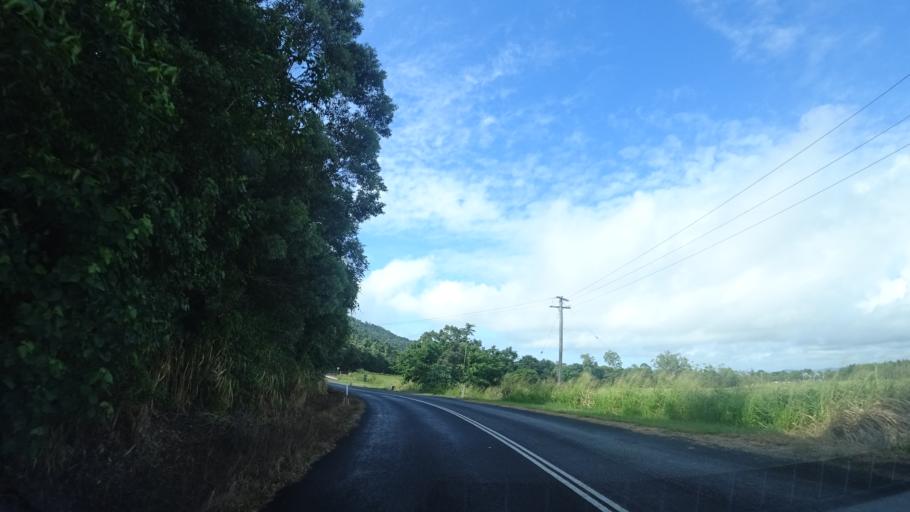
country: AU
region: Queensland
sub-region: Cassowary Coast
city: Innisfail
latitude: -17.5661
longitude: 146.0857
